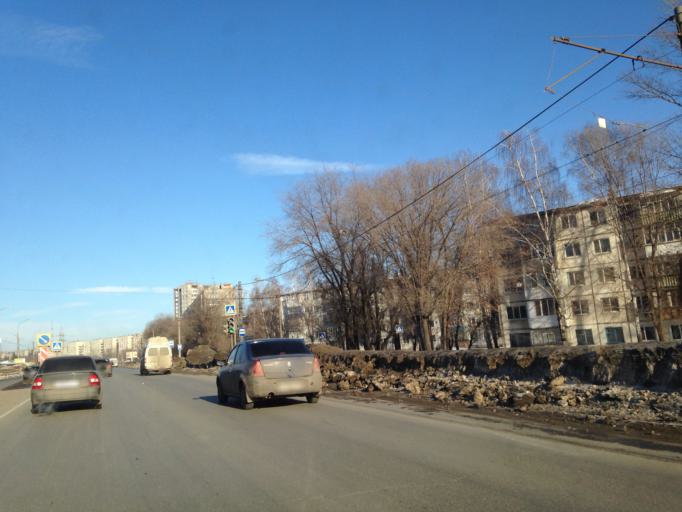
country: RU
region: Ulyanovsk
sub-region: Ulyanovskiy Rayon
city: Ulyanovsk
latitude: 54.3113
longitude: 48.3516
